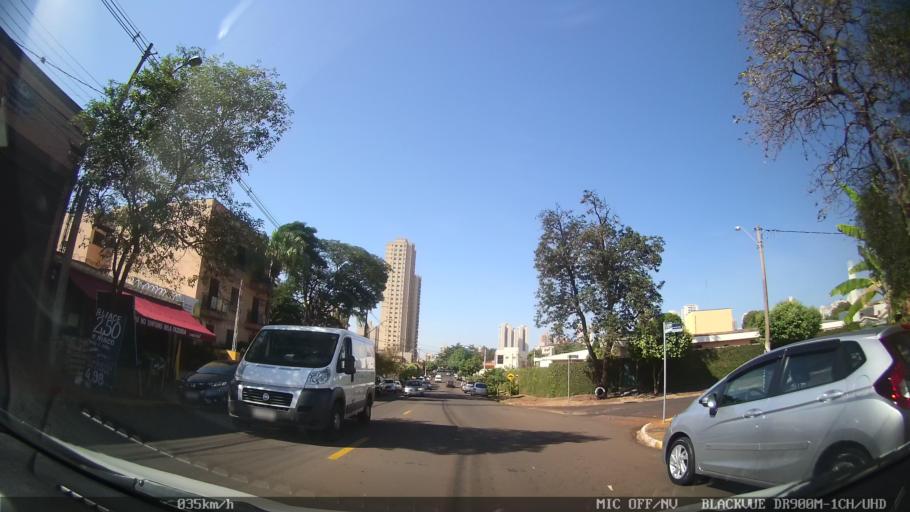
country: BR
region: Sao Paulo
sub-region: Ribeirao Preto
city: Ribeirao Preto
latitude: -21.2015
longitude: -47.8020
